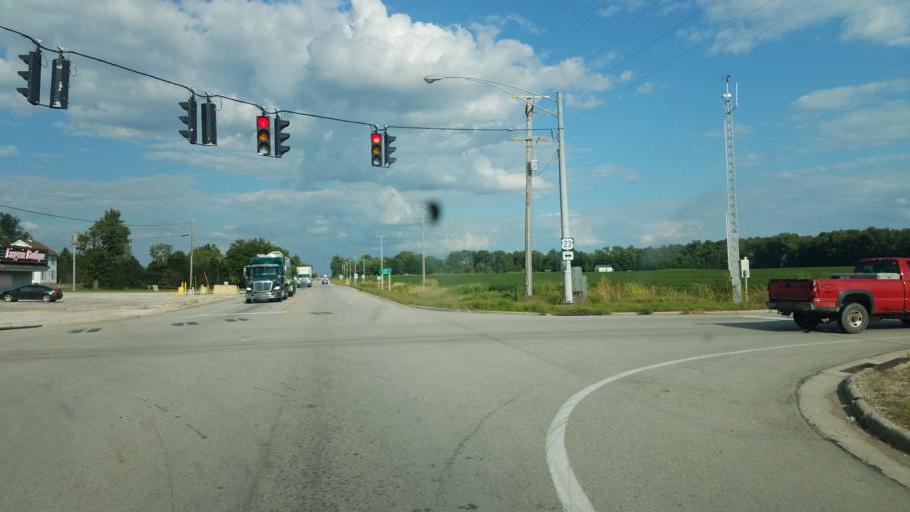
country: US
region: Ohio
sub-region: Wood County
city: Pemberville
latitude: 41.3413
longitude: -83.4176
